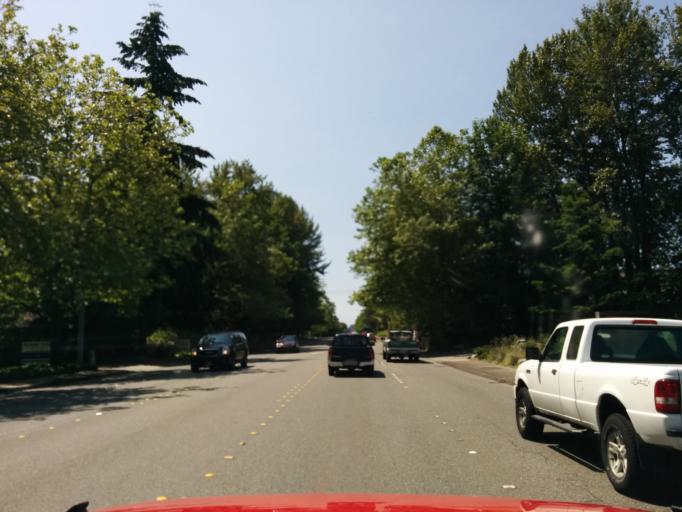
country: US
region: Washington
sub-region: King County
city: Bellevue
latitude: 47.6238
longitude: -122.1569
